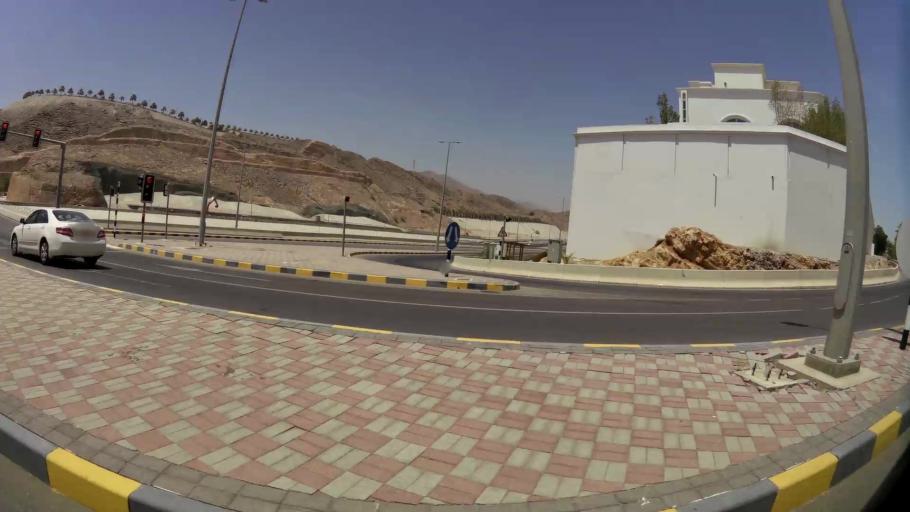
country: OM
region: Muhafazat Masqat
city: Bawshar
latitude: 23.5984
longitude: 58.4780
